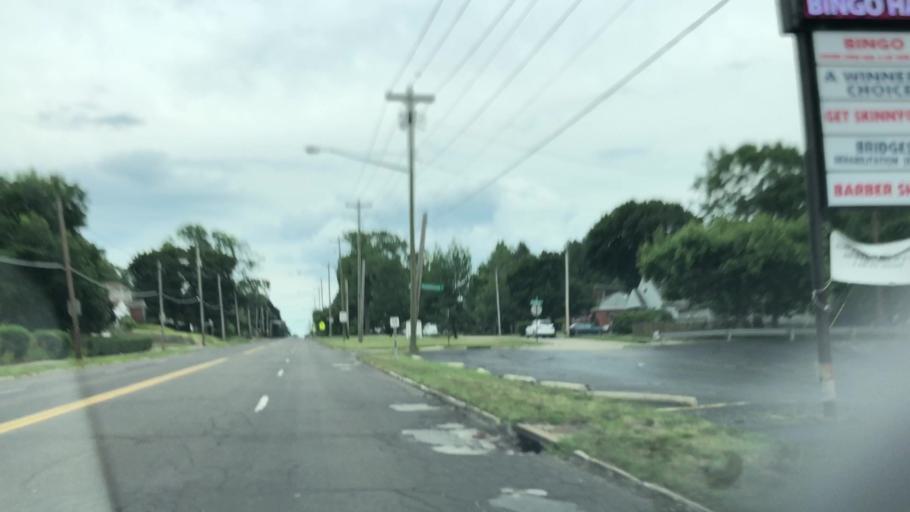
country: US
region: Ohio
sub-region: Summit County
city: Sawyerwood
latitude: 41.0585
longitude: -81.4499
